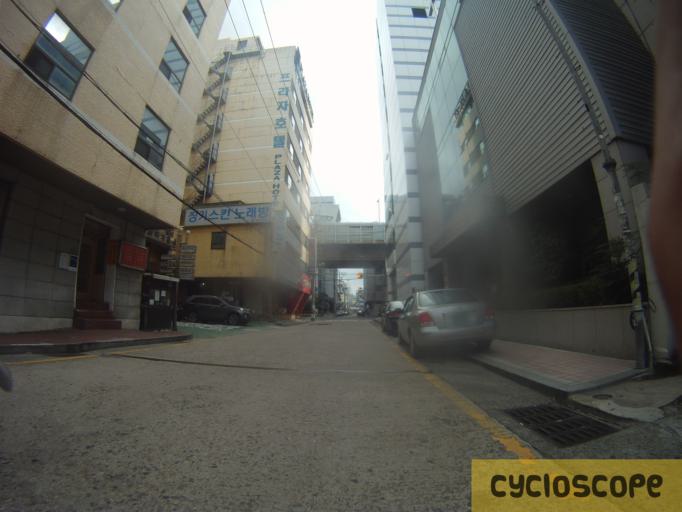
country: KR
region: Busan
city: Busan
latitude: 35.1095
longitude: 129.0387
